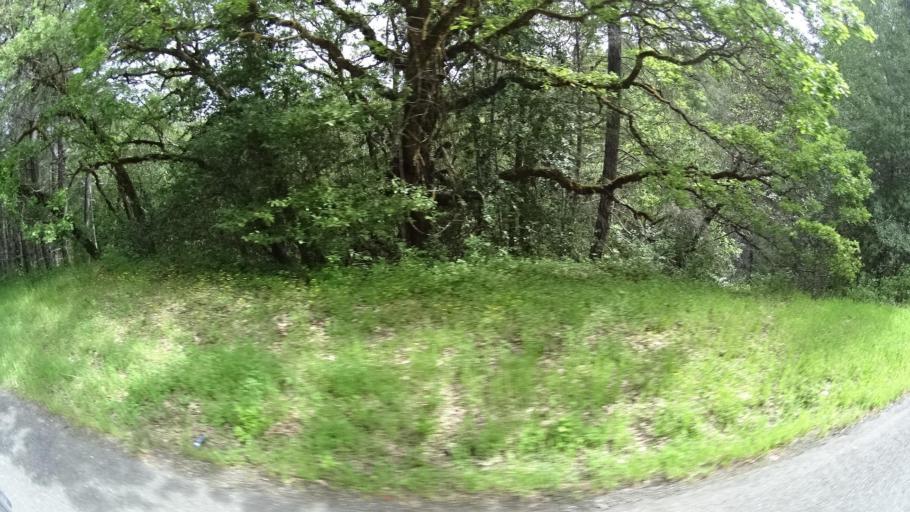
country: US
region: California
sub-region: Humboldt County
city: Redway
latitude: 40.1849
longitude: -123.5819
